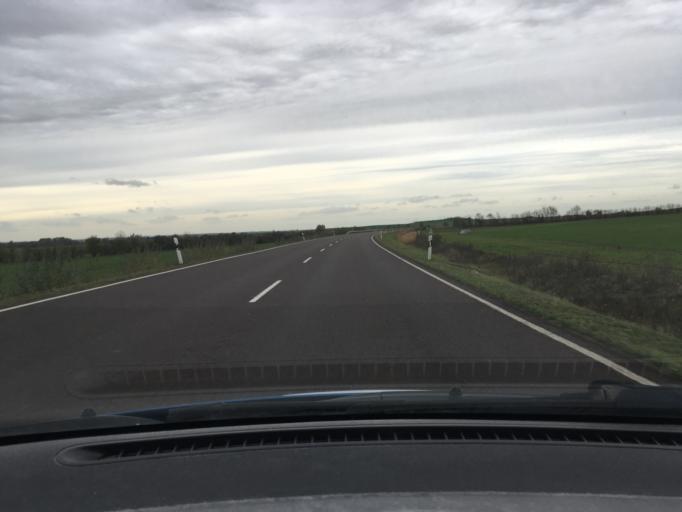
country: DE
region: Saxony-Anhalt
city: Leitzkau
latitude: 52.0517
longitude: 11.9447
